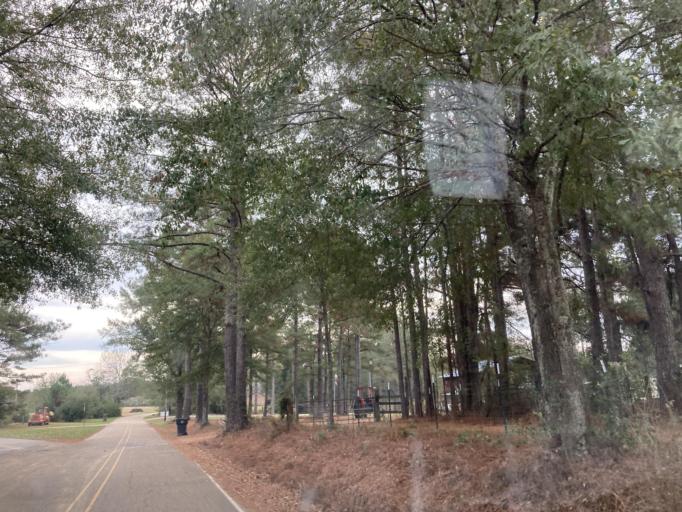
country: US
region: Mississippi
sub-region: Lamar County
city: Purvis
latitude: 31.0970
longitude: -89.4684
